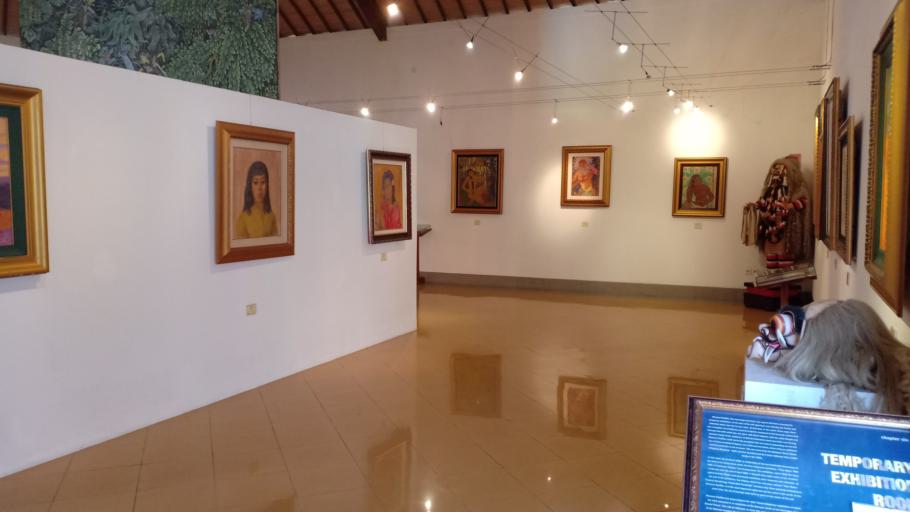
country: ID
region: Bali
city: Bualu
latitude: -8.7998
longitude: 115.2306
